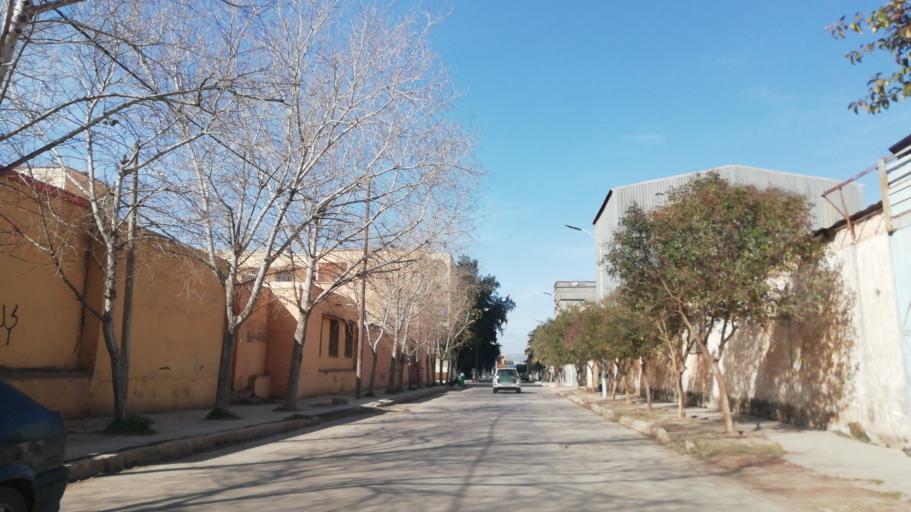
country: DZ
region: Oran
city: Es Senia
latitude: 35.6118
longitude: -0.5755
